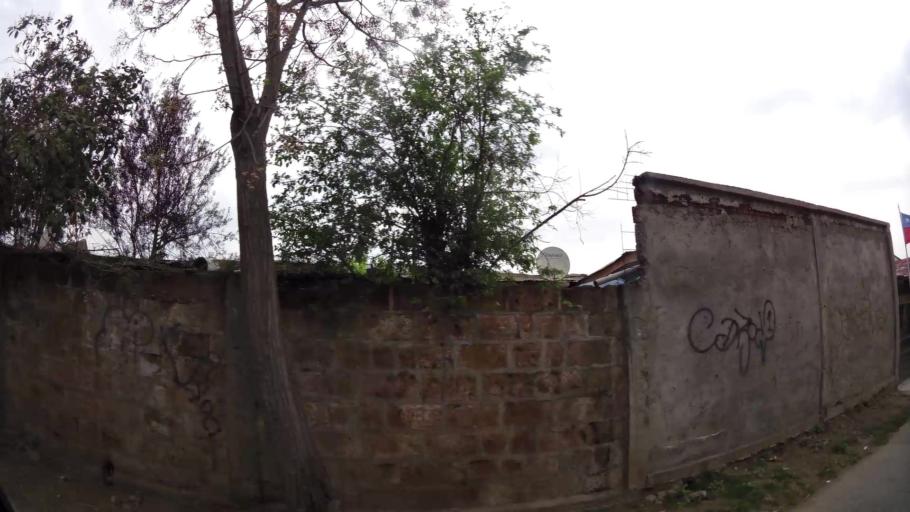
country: CL
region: Santiago Metropolitan
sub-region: Provincia de Santiago
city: Lo Prado
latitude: -33.5019
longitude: -70.7724
